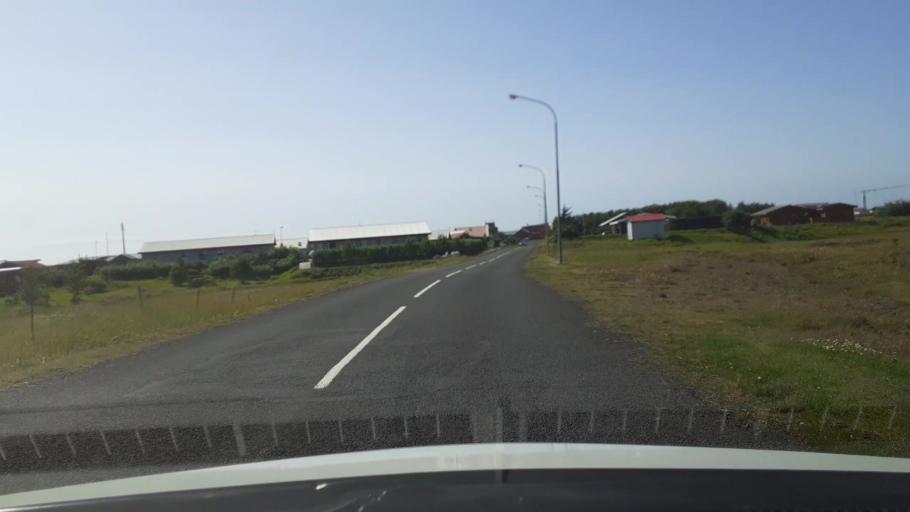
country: IS
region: South
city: Selfoss
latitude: 63.8394
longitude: -21.0557
